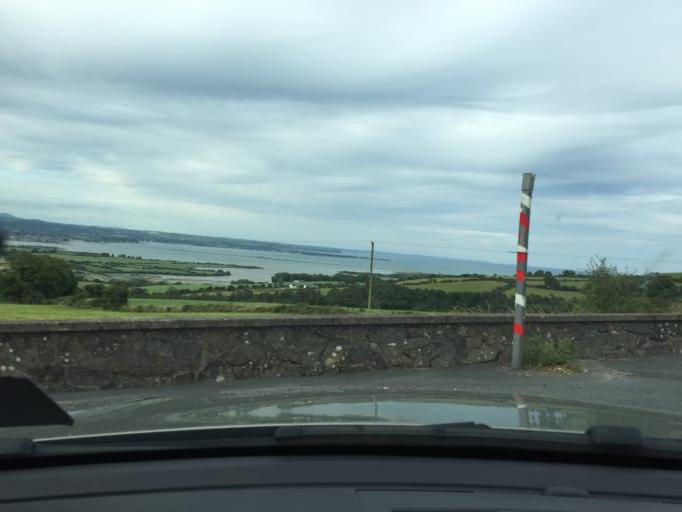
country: IE
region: Munster
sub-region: Waterford
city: Dungarvan
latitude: 52.0518
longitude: -7.6632
